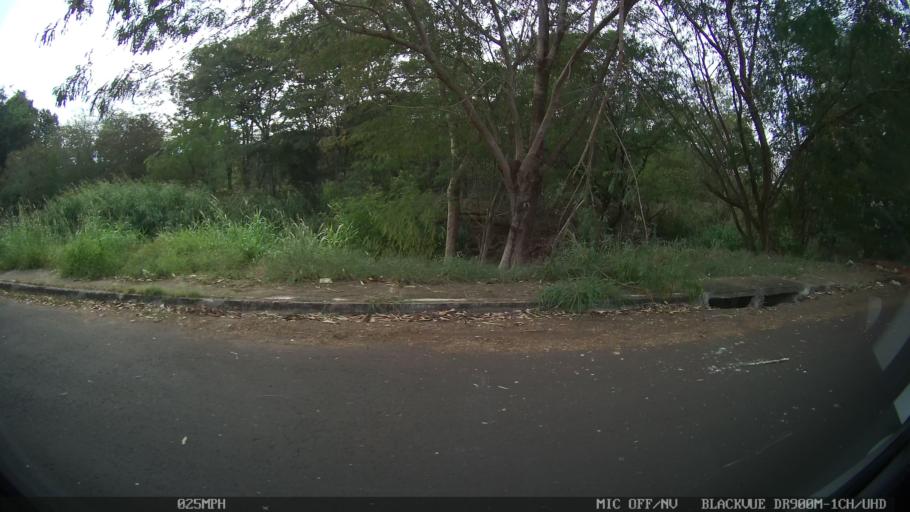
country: BR
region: Sao Paulo
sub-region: Catanduva
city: Catanduva
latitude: -21.1252
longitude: -48.9810
